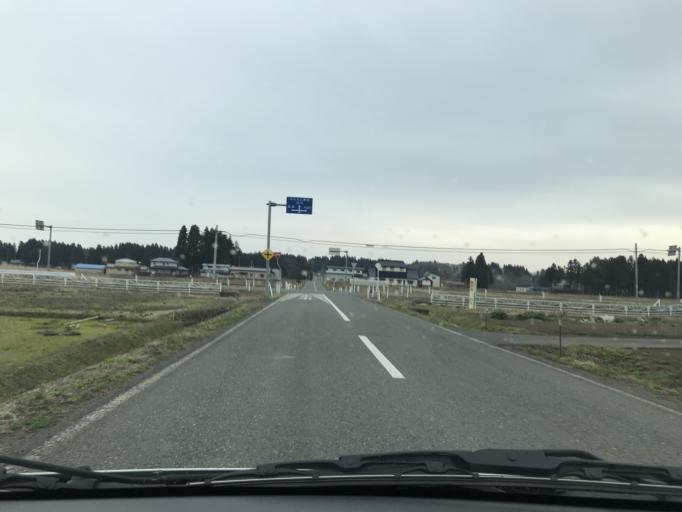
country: JP
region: Iwate
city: Mizusawa
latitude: 39.0995
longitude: 141.0695
